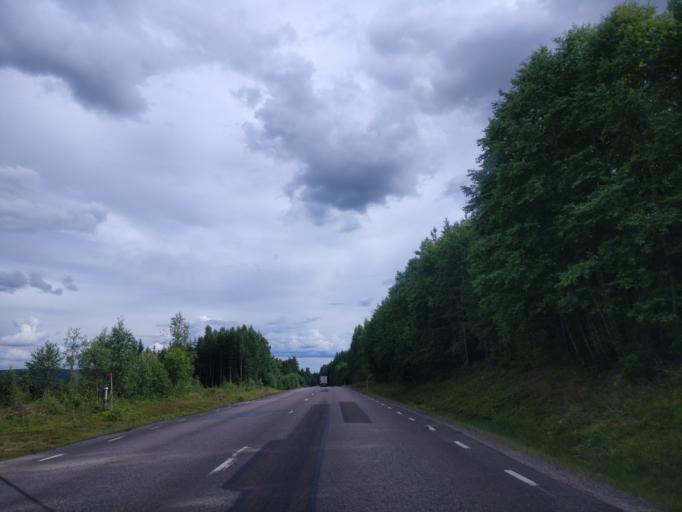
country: SE
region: Vaermland
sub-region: Hagfors Kommun
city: Ekshaerad
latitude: 60.1497
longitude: 13.5199
